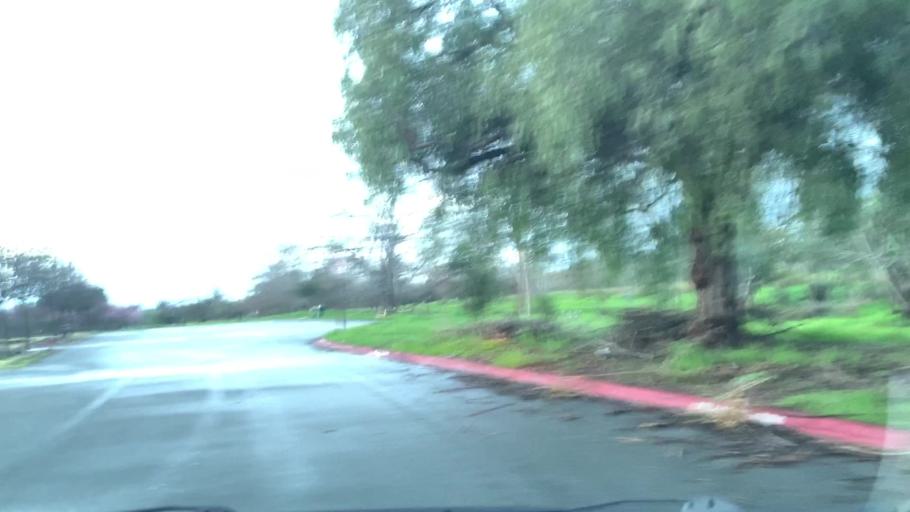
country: US
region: California
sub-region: Santa Clara County
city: Seven Trees
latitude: 37.3203
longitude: -121.8547
